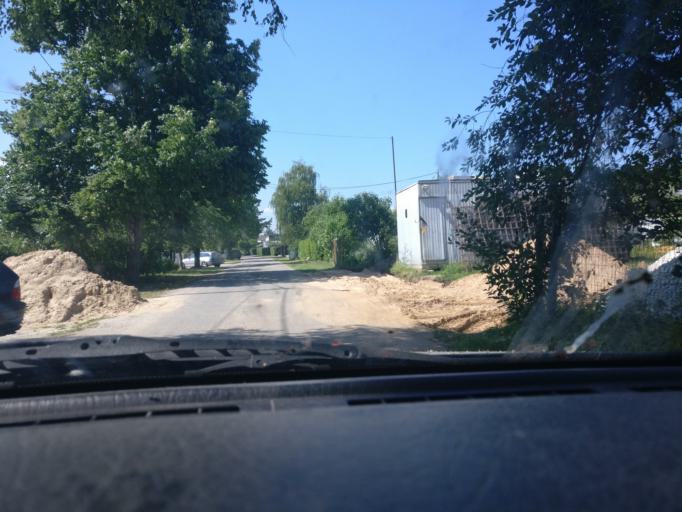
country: EE
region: Tartu
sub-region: UElenurme vald
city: Ulenurme
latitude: 58.3470
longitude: 26.7906
